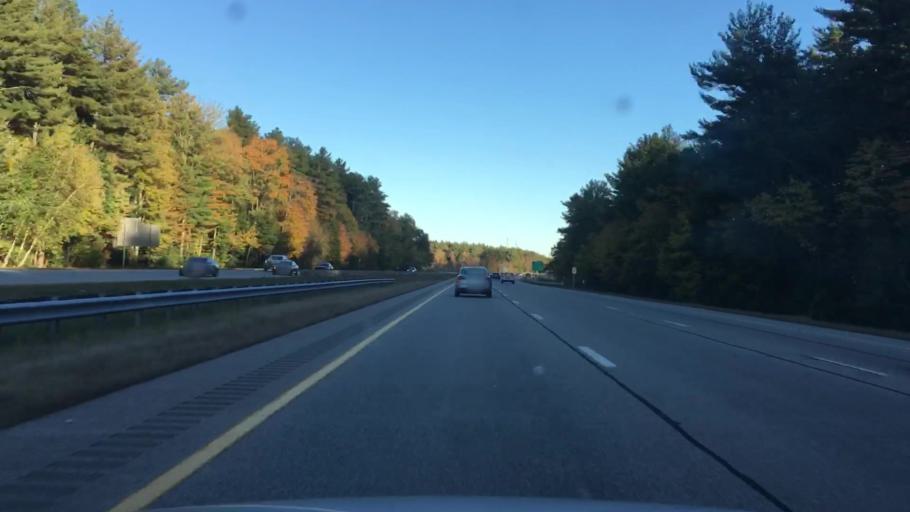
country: US
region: New Hampshire
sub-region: Rockingham County
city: Epping
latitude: 43.0254
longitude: -71.0680
